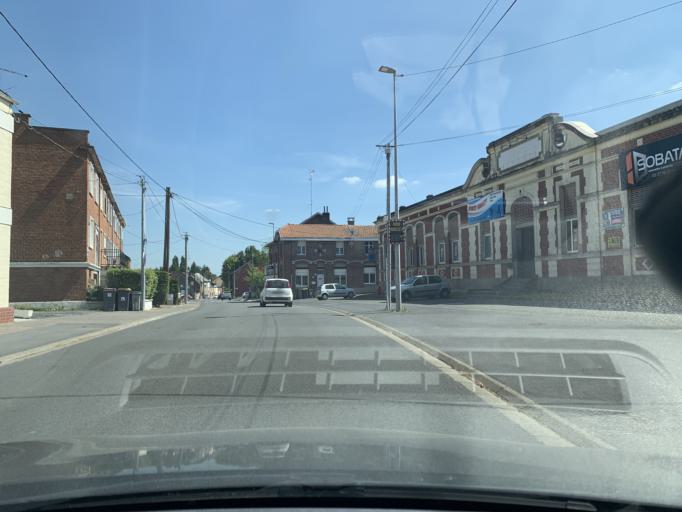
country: FR
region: Nord-Pas-de-Calais
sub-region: Departement du Nord
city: Caudry
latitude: 50.1250
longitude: 3.3977
